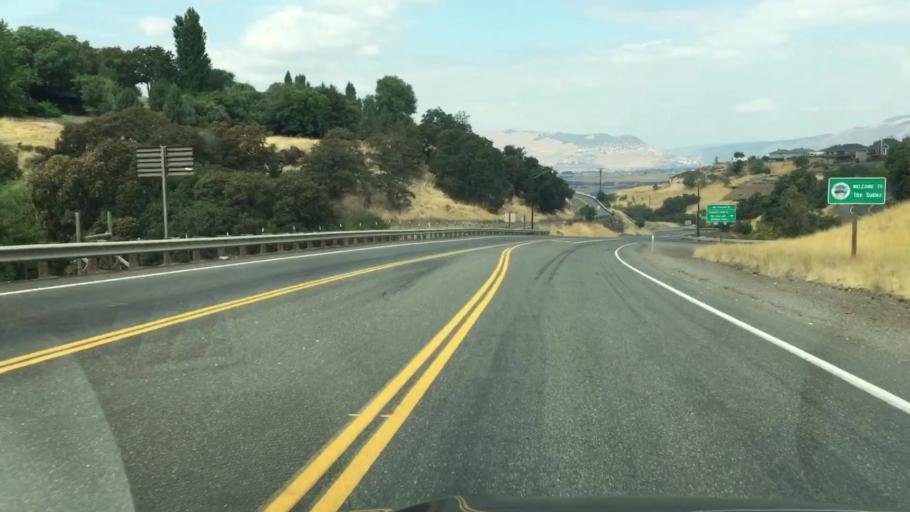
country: US
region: Oregon
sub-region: Wasco County
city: The Dalles
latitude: 45.5955
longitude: -121.1335
